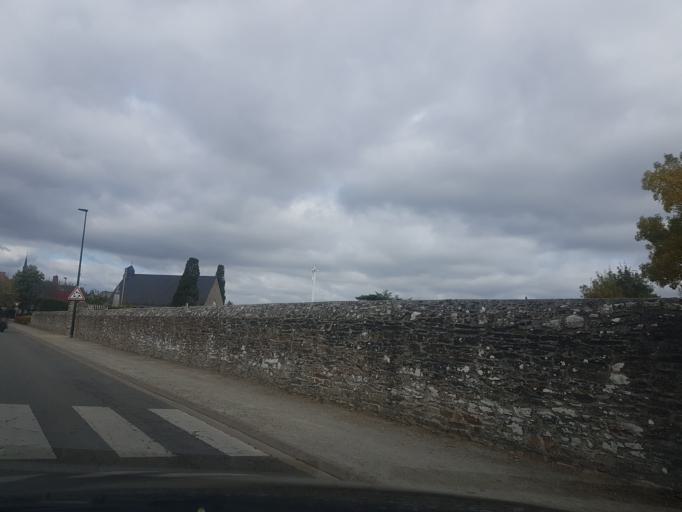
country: FR
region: Pays de la Loire
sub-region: Departement de la Loire-Atlantique
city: Ligne
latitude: 47.4103
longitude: -1.3745
